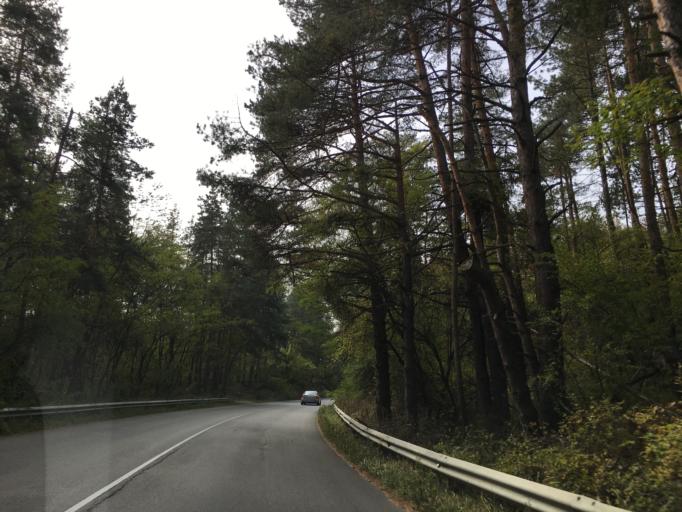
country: BG
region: Sofiya
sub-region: Obshtina Samokov
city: Samokov
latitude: 42.4518
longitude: 23.5564
